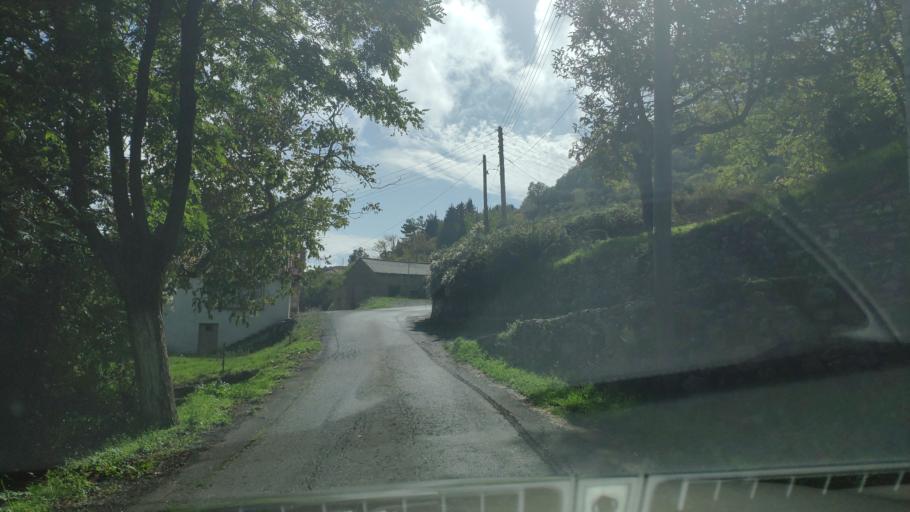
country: GR
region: Peloponnese
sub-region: Nomos Arkadias
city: Dimitsana
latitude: 37.5888
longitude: 22.0211
